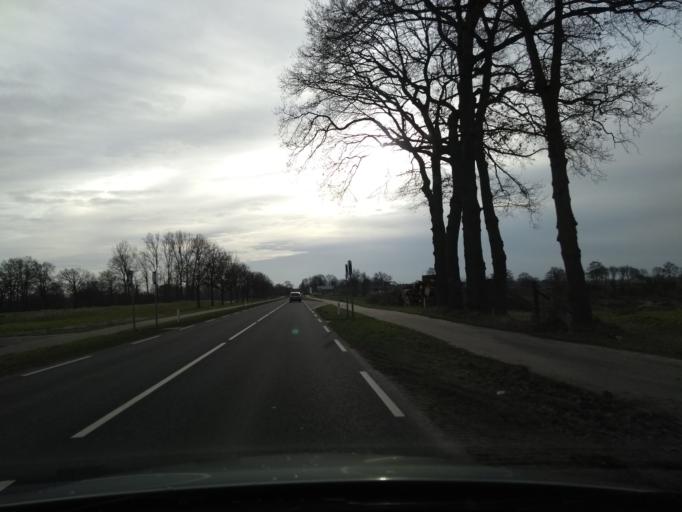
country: NL
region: Overijssel
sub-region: Gemeente Almelo
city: Almelo
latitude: 52.3183
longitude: 6.6546
